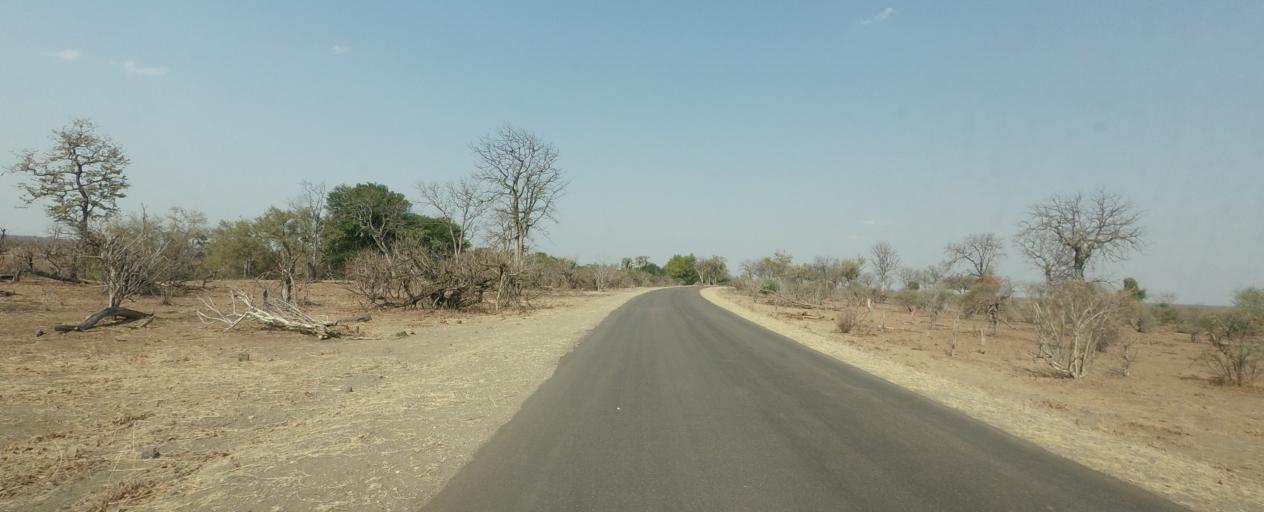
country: ZA
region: Limpopo
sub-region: Mopani District Municipality
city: Giyani
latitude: -23.0967
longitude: 31.3918
